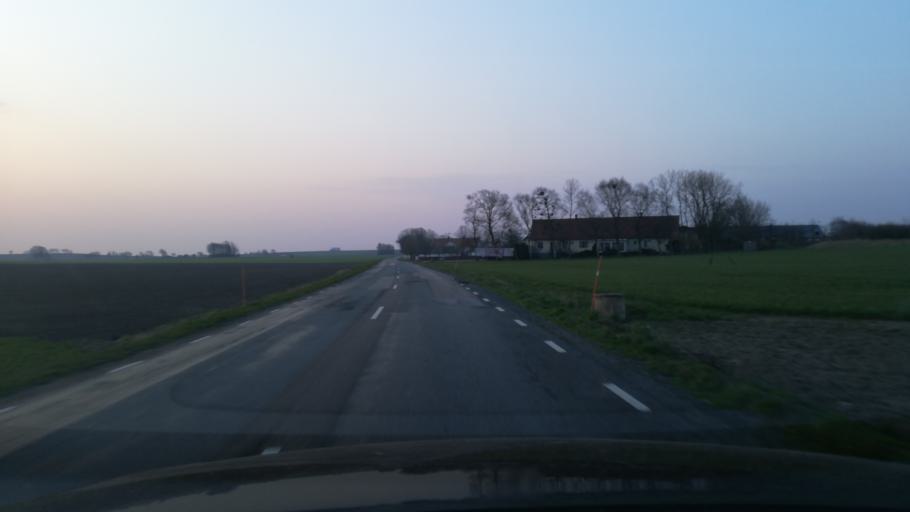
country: SE
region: Skane
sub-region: Ystads Kommun
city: Kopingebro
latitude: 55.4562
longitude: 14.1112
